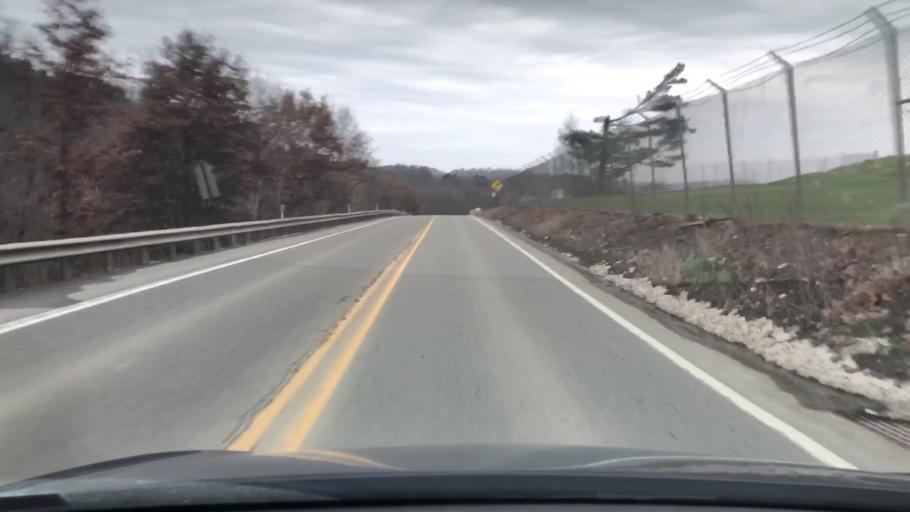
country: US
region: Pennsylvania
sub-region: Clarion County
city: Clarion
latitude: 41.0127
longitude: -79.2809
